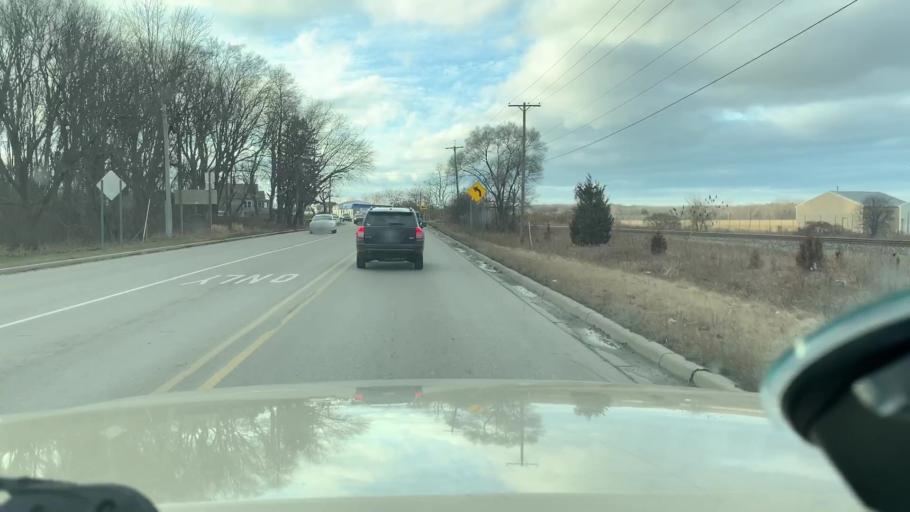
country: US
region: Michigan
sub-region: Jackson County
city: Jackson
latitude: 42.2543
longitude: -84.4625
